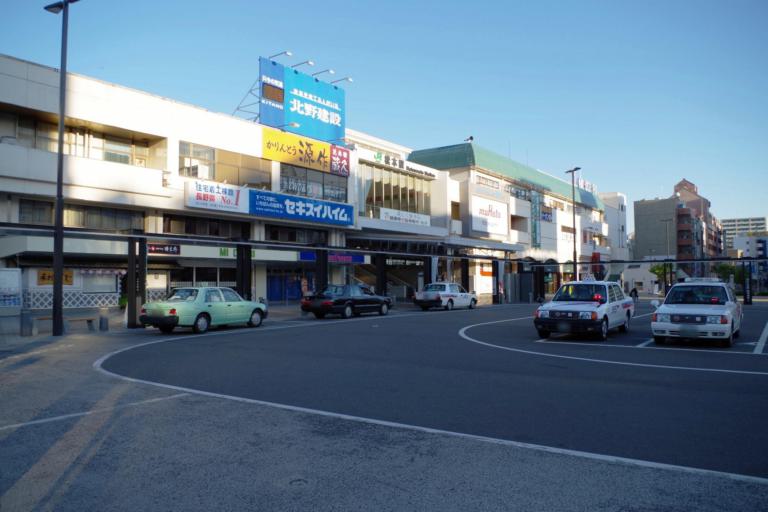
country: JP
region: Nagano
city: Matsumoto
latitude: 36.2307
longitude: 137.9653
